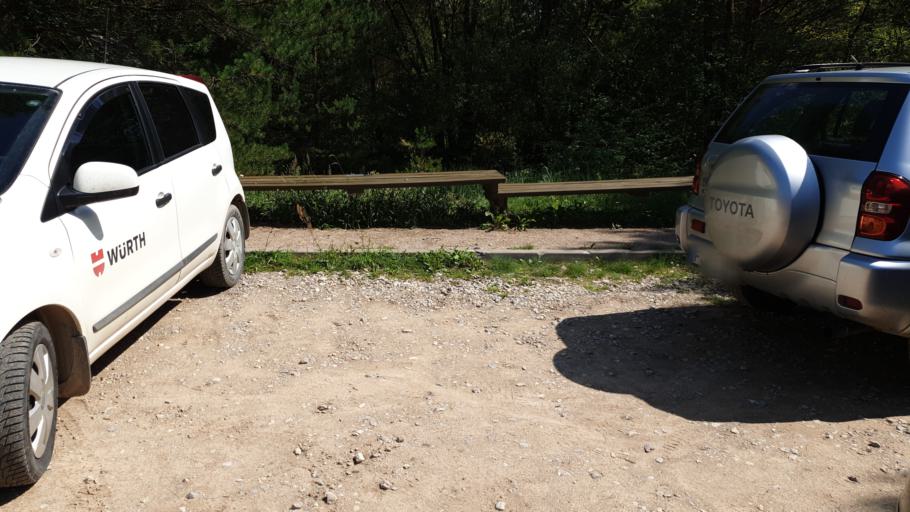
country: LT
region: Vilnius County
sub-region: Vilniaus Rajonas
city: Vievis
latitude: 54.8267
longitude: 24.9464
